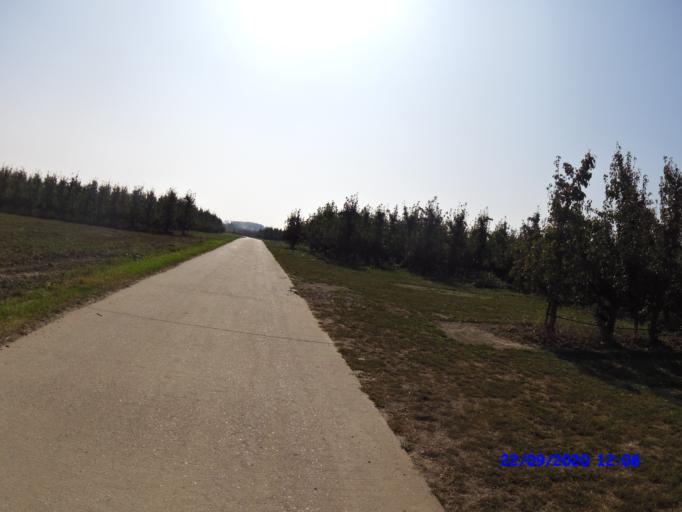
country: BE
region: Flanders
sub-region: Provincie Limburg
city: Alken
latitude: 50.8546
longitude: 5.3017
